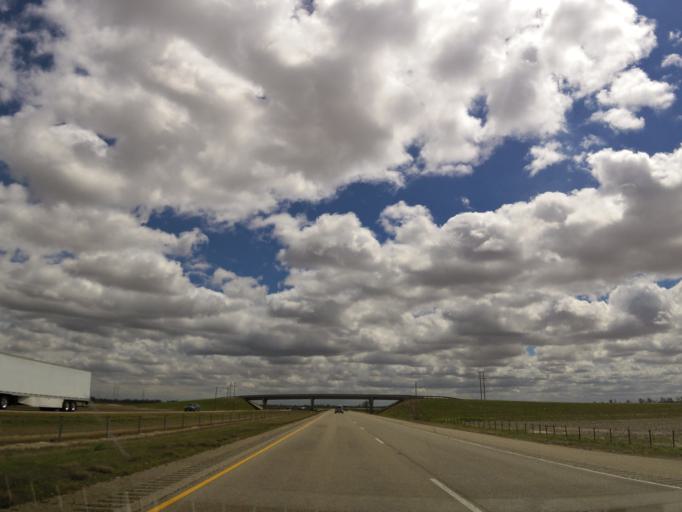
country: US
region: Arkansas
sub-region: Craighead County
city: Bay
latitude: 35.7071
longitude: -90.5686
